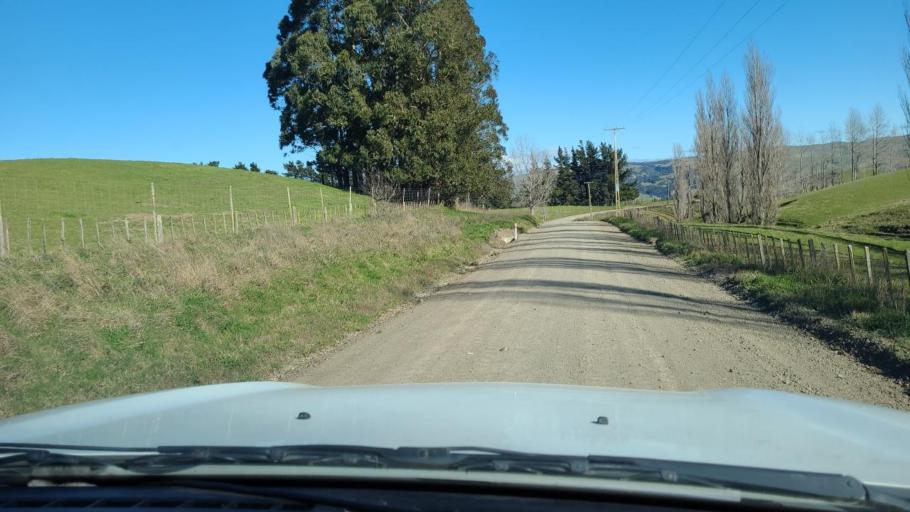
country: NZ
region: Hawke's Bay
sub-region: Napier City
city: Taradale
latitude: -39.4936
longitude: 176.4854
